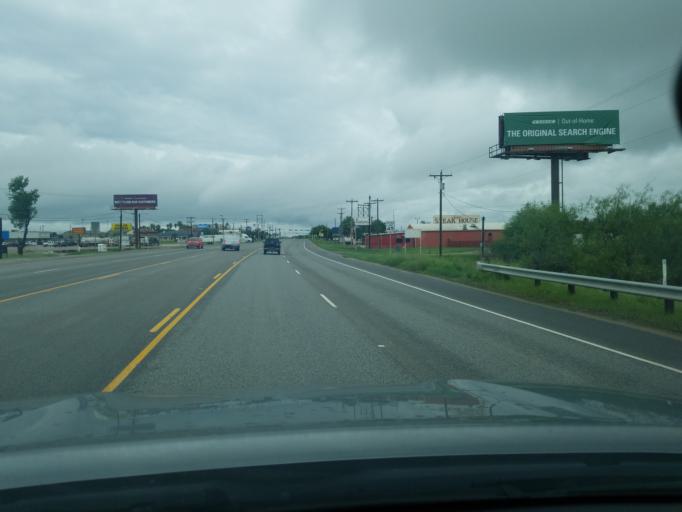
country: US
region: Texas
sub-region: Dimmit County
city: Carrizo Springs
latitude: 28.5400
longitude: -99.8490
